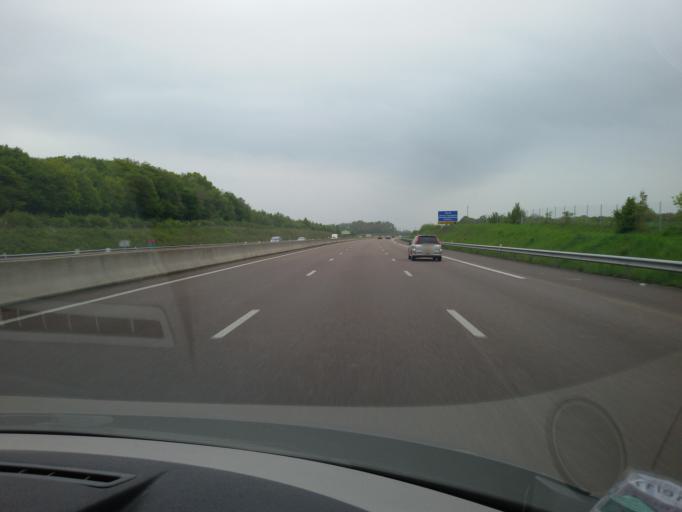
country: FR
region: Bourgogne
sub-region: Departement de la Cote-d'Or
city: Gevrey-Chambertin
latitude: 47.2018
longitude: 4.9968
